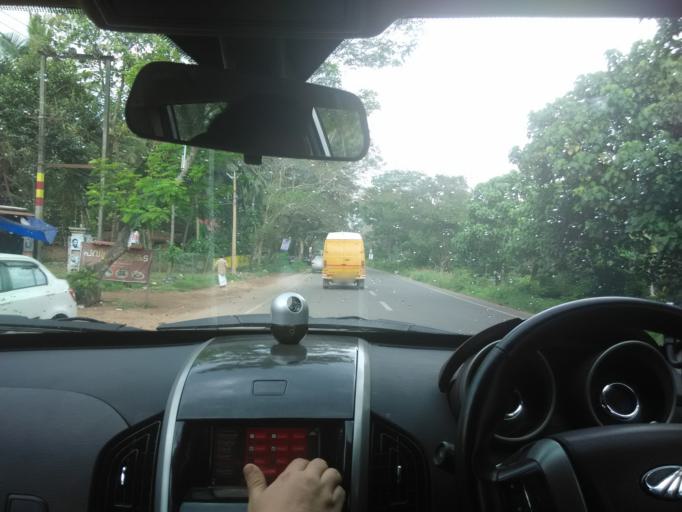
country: IN
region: Kerala
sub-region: Thiruvananthapuram
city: Attingal
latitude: 8.6443
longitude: 76.8431
